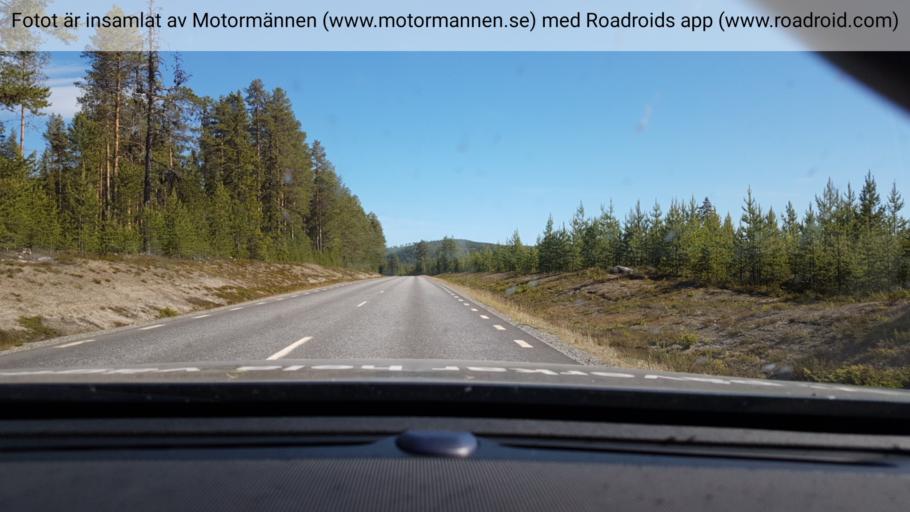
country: SE
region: Vaesterbotten
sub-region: Lycksele Kommun
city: Soderfors
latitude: 64.7325
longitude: 18.2124
